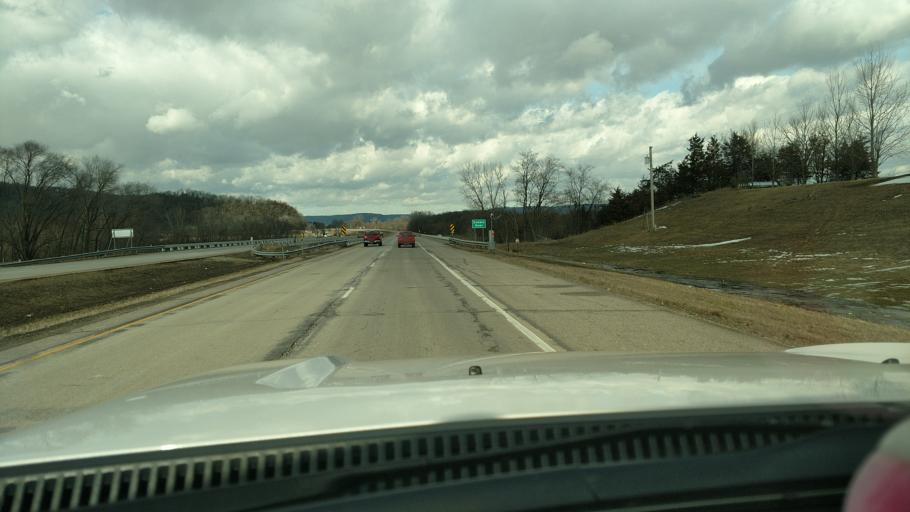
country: US
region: Minnesota
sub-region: Wabasha County
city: Wabasha
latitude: 44.3108
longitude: -92.0039
